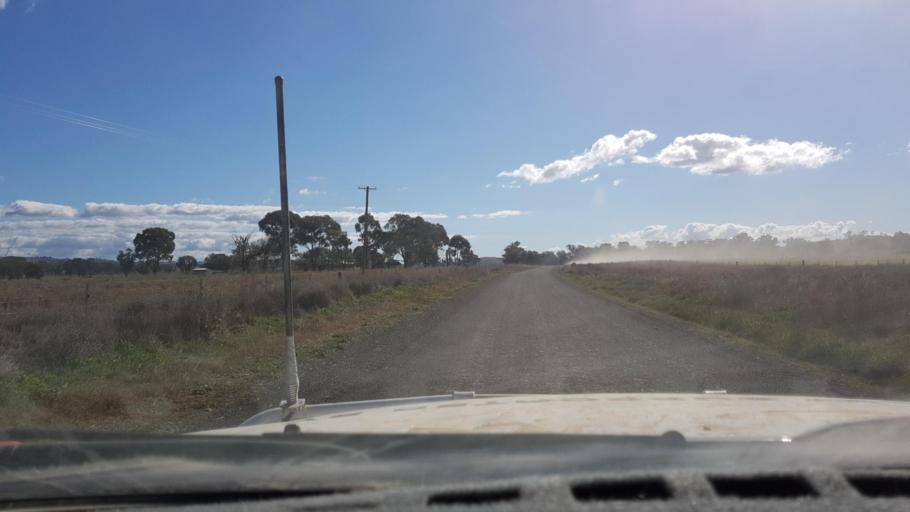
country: AU
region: New South Wales
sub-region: Narrabri
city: Blair Athol
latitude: -30.5261
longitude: 150.4432
